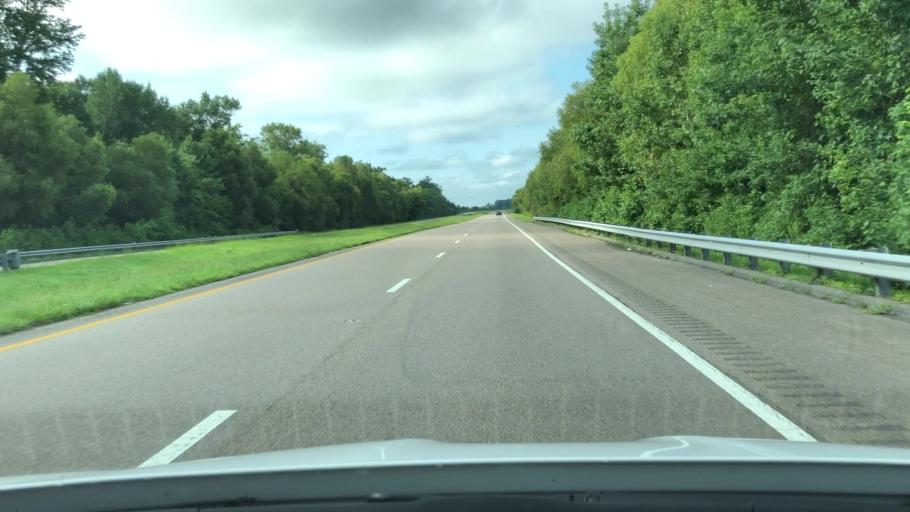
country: US
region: Virginia
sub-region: City of Portsmouth
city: Portsmouth Heights
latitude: 36.6301
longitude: -76.3642
